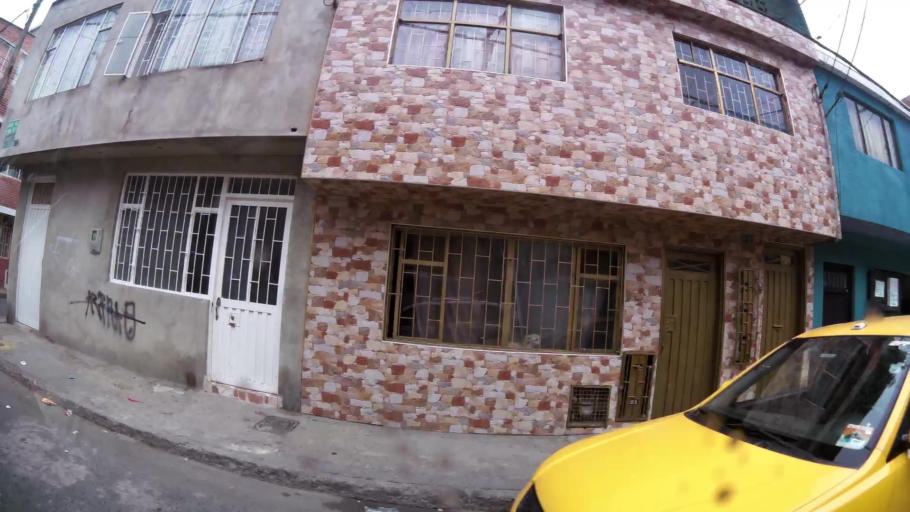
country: CO
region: Bogota D.C.
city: Bogota
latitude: 4.6043
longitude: -74.1370
